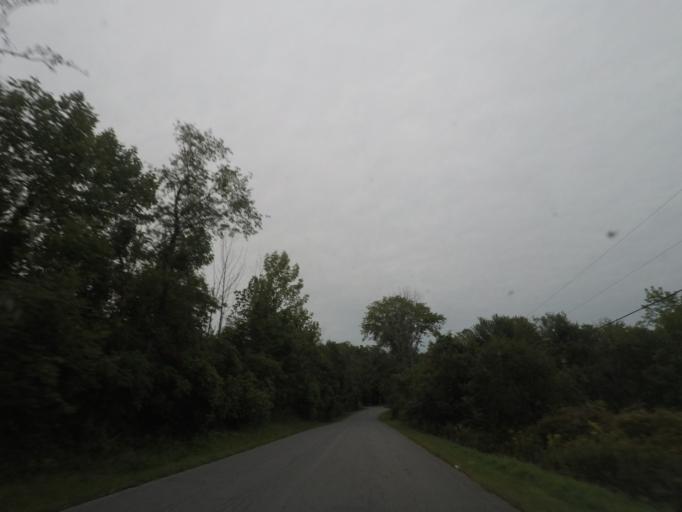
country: US
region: New York
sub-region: Rensselaer County
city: West Sand Lake
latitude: 42.5872
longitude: -73.6110
